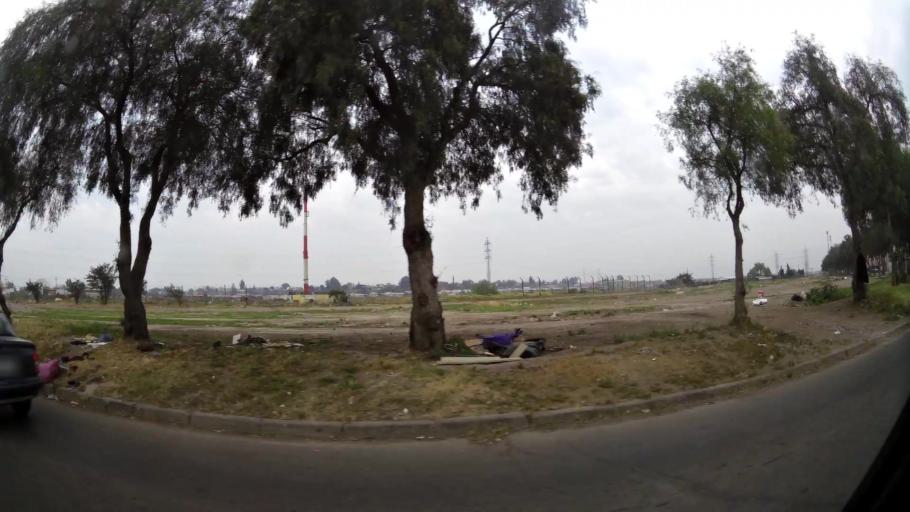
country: CL
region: Santiago Metropolitan
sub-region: Provincia de Santiago
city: Lo Prado
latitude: -33.4815
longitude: -70.7262
